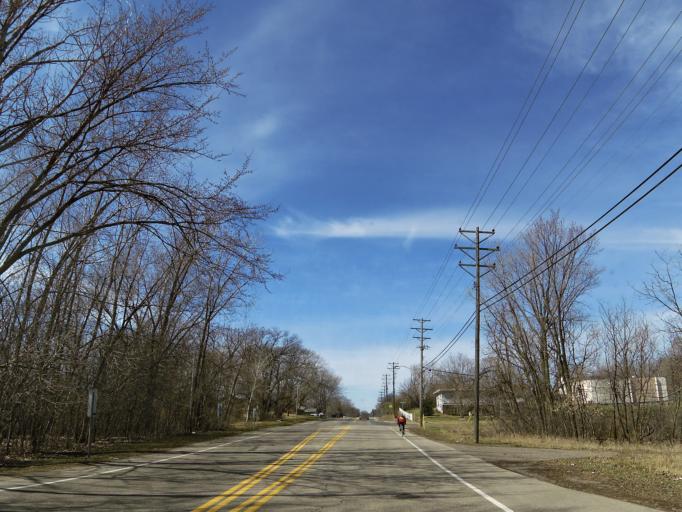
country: US
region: Minnesota
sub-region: Ramsey County
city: North Saint Paul
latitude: 44.9921
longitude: -93.0103
